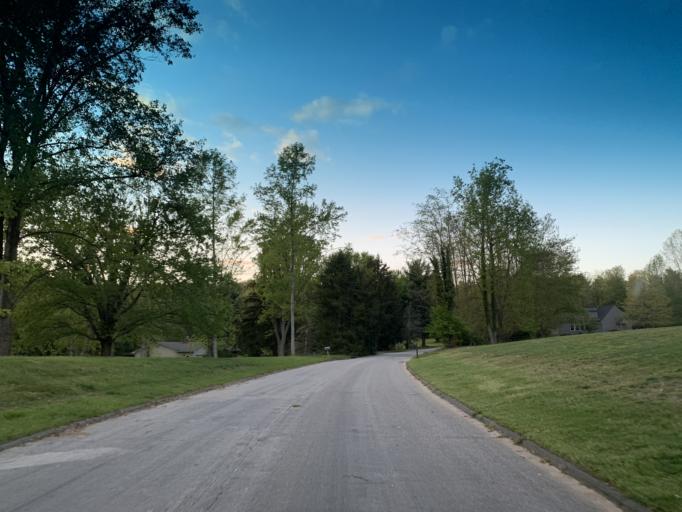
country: US
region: Pennsylvania
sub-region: York County
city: Susquehanna Trails
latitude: 39.6872
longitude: -76.3511
